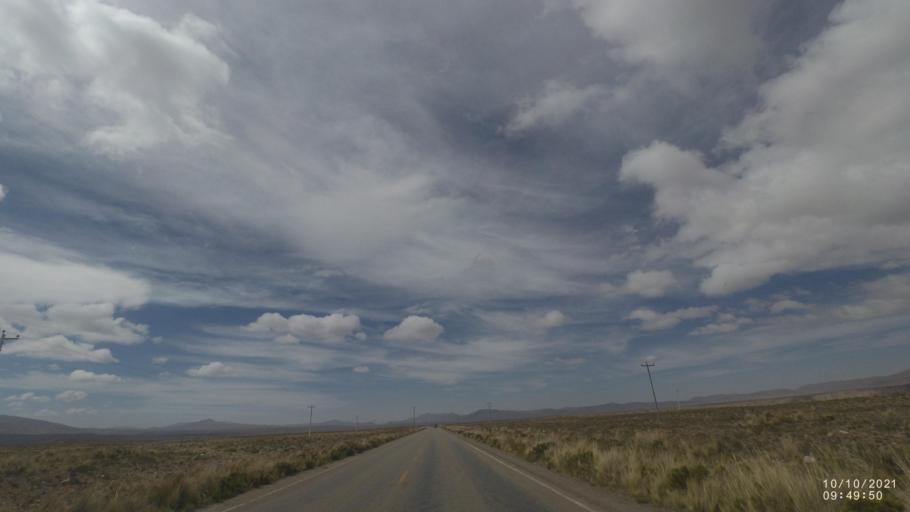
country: BO
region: La Paz
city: Colquiri
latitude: -17.2331
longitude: -67.3357
